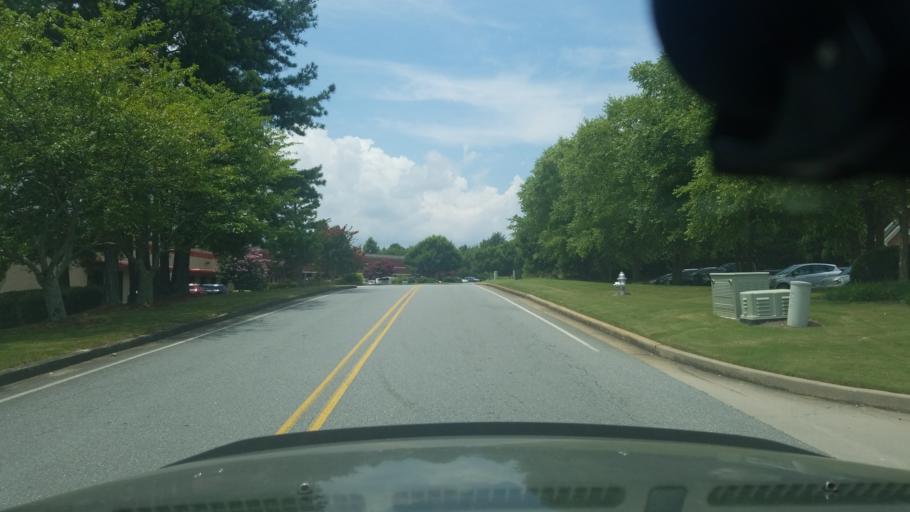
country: US
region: Georgia
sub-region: Fulton County
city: Milton
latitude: 34.1431
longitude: -84.2475
